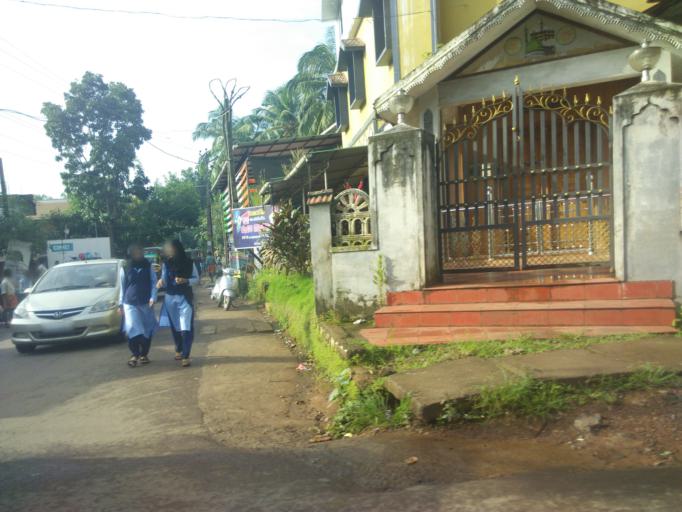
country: IN
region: Kerala
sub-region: Kozhikode
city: Kunnamangalam
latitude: 11.2968
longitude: 75.8349
